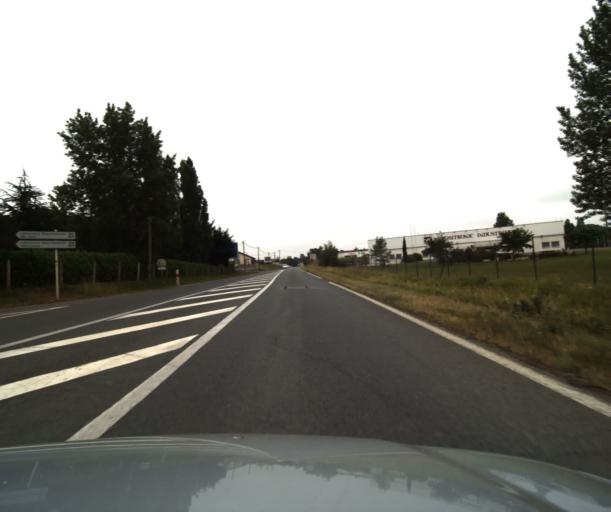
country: FR
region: Midi-Pyrenees
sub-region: Departement du Gers
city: Auch
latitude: 43.6572
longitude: 0.6273
